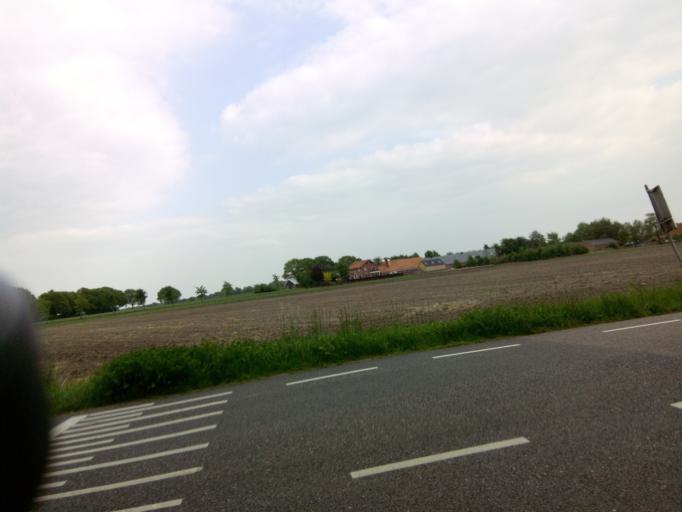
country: NL
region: Gelderland
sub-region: Berkelland
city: Eibergen
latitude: 52.0842
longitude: 6.6153
